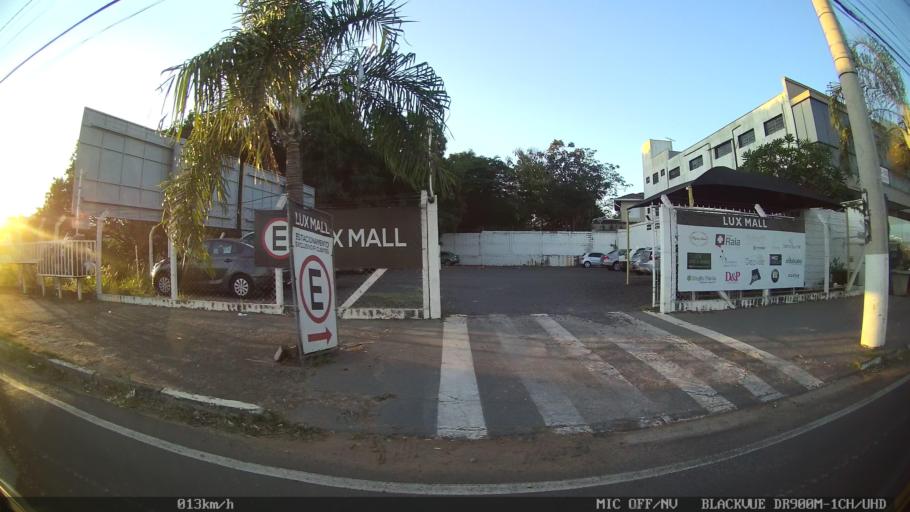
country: BR
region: Sao Paulo
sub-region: Sao Jose Do Rio Preto
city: Sao Jose do Rio Preto
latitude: -20.8089
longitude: -49.3540
